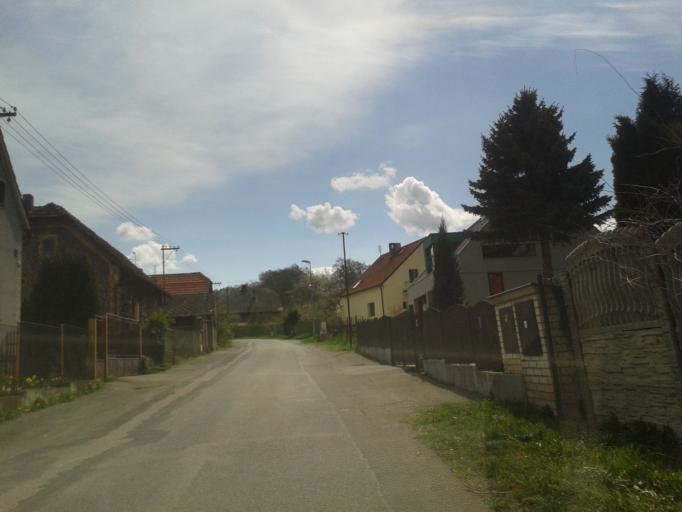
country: CZ
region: Central Bohemia
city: Dobris
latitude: 49.8691
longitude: 14.1415
